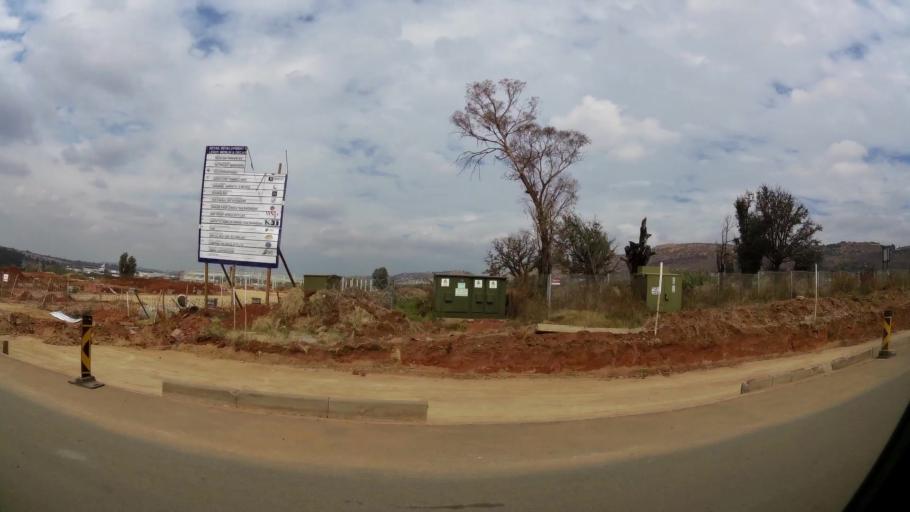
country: ZA
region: Gauteng
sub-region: City of Johannesburg Metropolitan Municipality
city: Roodepoort
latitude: -26.1095
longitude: 27.8871
